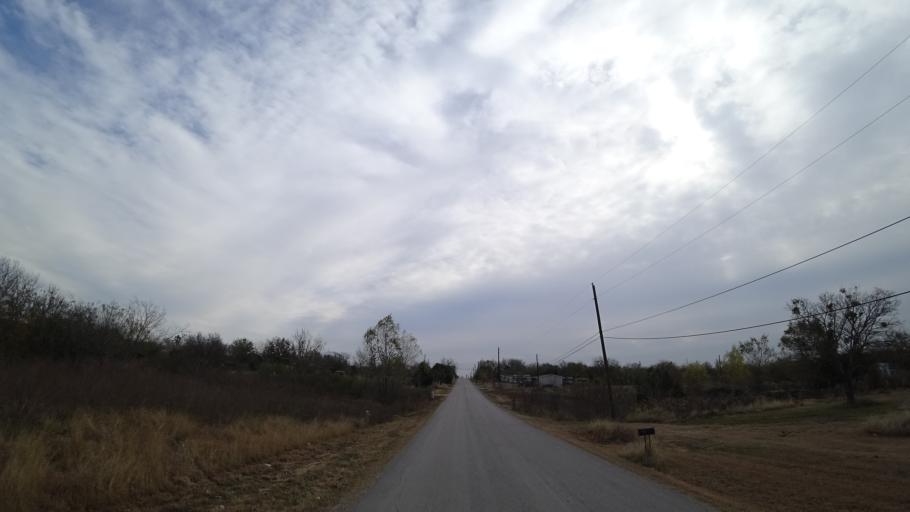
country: US
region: Texas
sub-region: Travis County
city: Onion Creek
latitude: 30.1487
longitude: -97.6703
